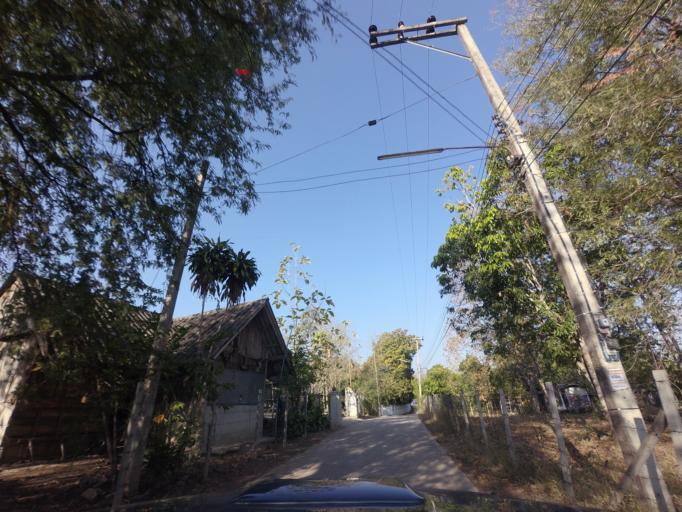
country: TH
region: Chiang Mai
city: San Sai
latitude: 18.9004
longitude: 99.1143
